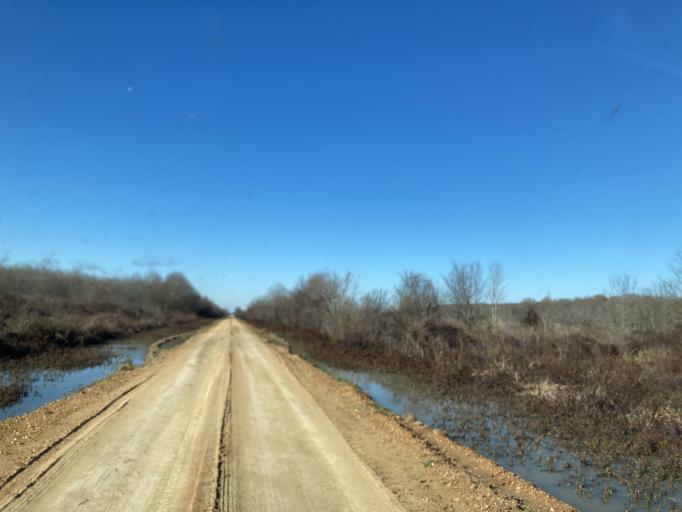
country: US
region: Mississippi
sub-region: Yazoo County
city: Yazoo City
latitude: 32.9518
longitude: -90.6229
